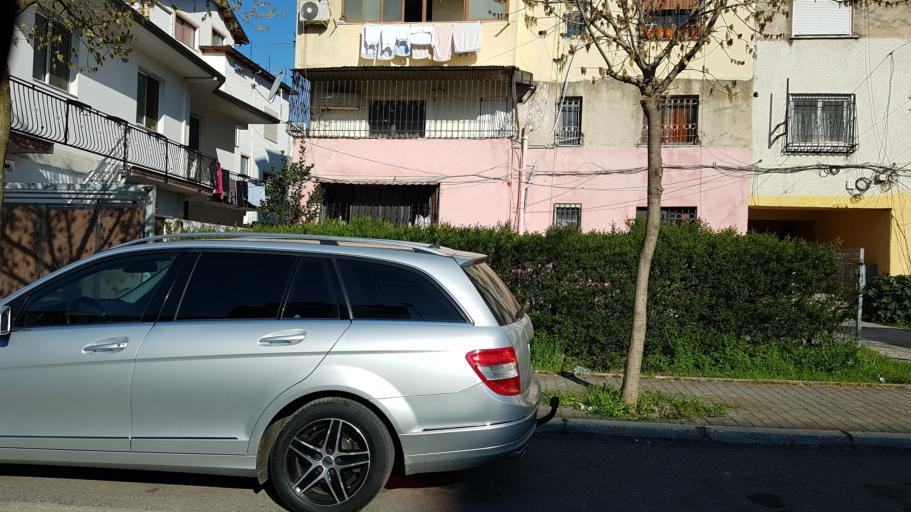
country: AL
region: Shkoder
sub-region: Rrethi i Shkodres
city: Shkoder
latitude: 42.0651
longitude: 19.5028
